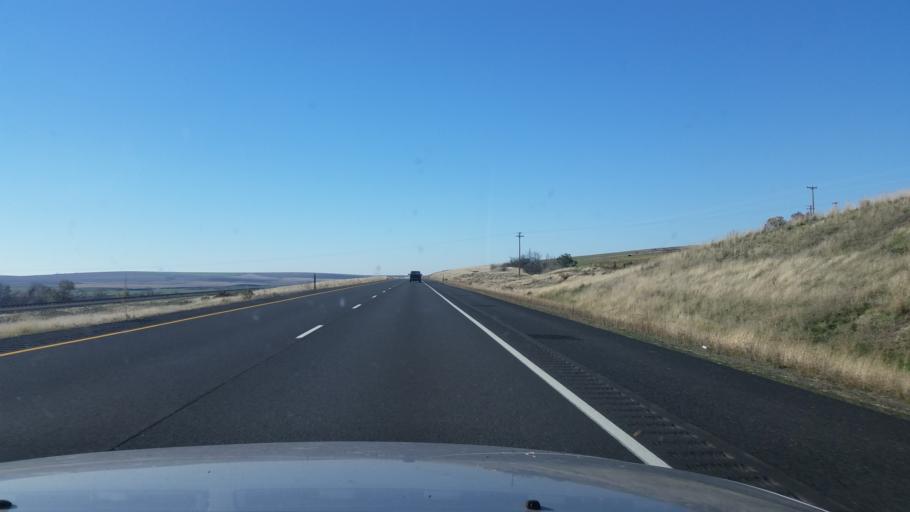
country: US
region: Washington
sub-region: Grant County
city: Warden
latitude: 47.0868
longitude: -118.9371
